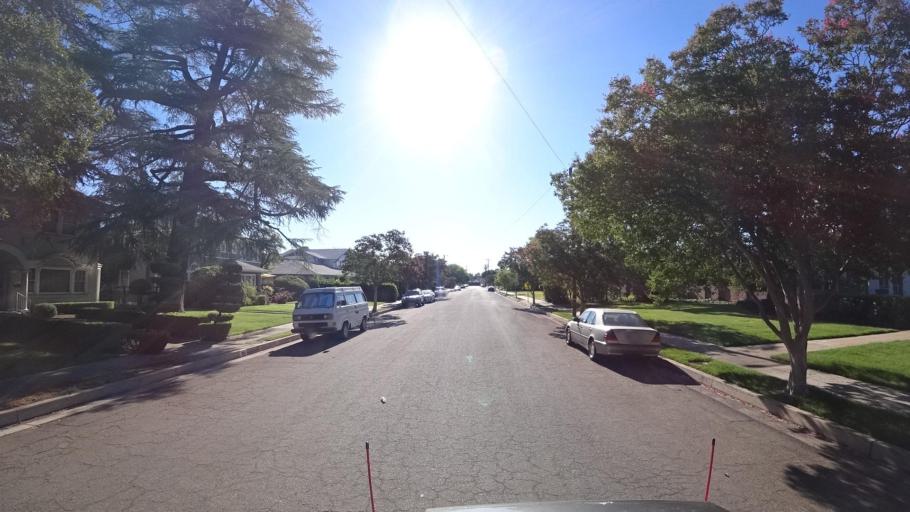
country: US
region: California
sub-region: Fresno County
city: Fresno
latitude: 36.7623
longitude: -119.8027
